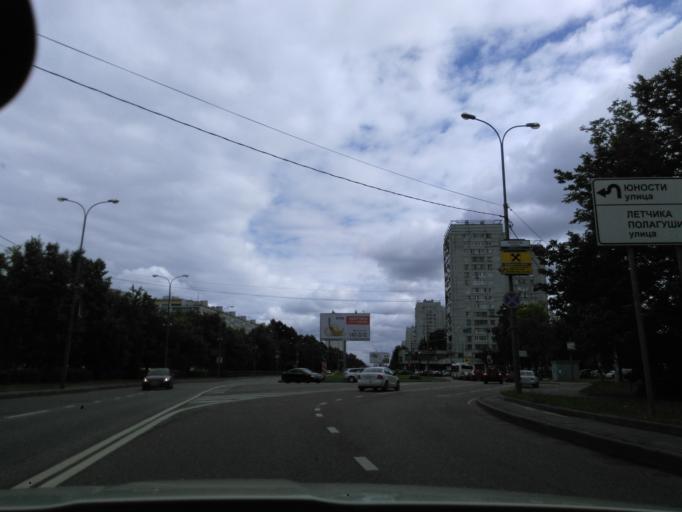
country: RU
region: Moskovskaya
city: Mendeleyevo
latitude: 56.0025
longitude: 37.2081
